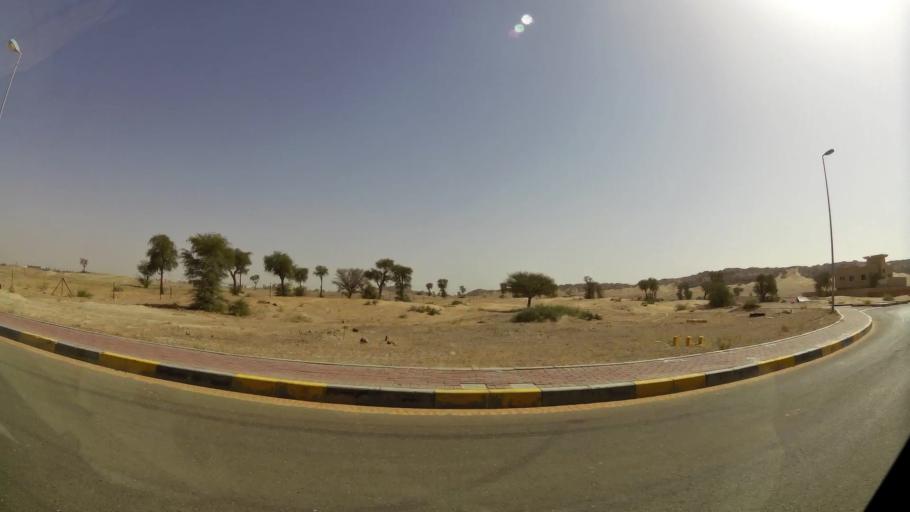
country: OM
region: Al Buraimi
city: Al Buraymi
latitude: 24.3222
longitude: 55.8092
